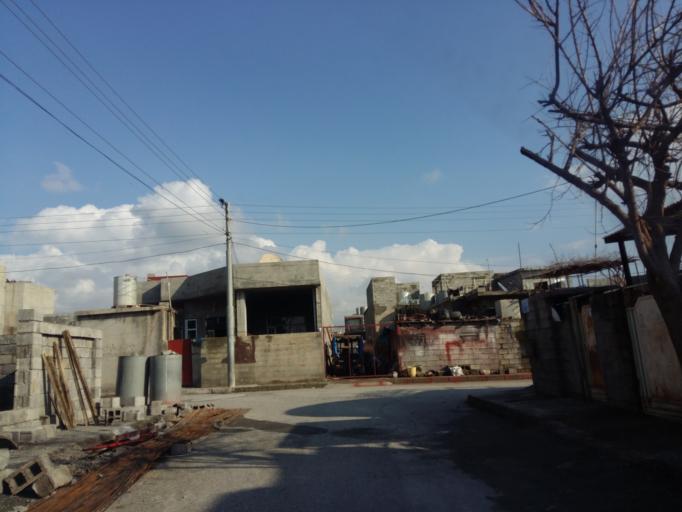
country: IQ
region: As Sulaymaniyah
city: Qeladize
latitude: 36.1766
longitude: 45.1397
